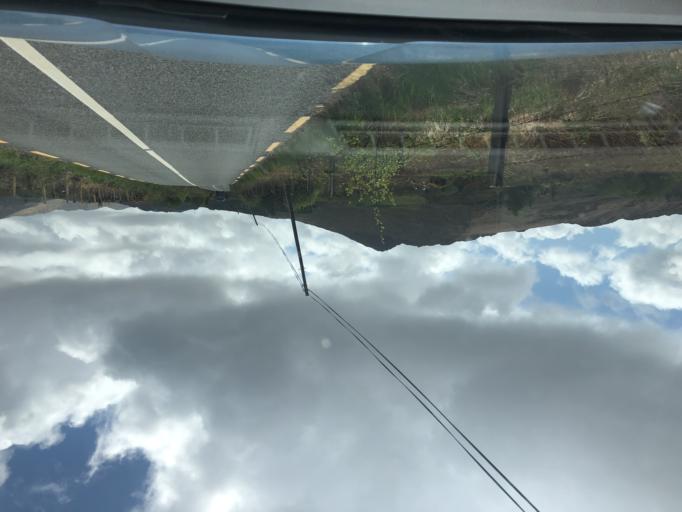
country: IE
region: Munster
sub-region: Ciarrai
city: Killorglin
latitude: 51.8316
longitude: -9.9297
